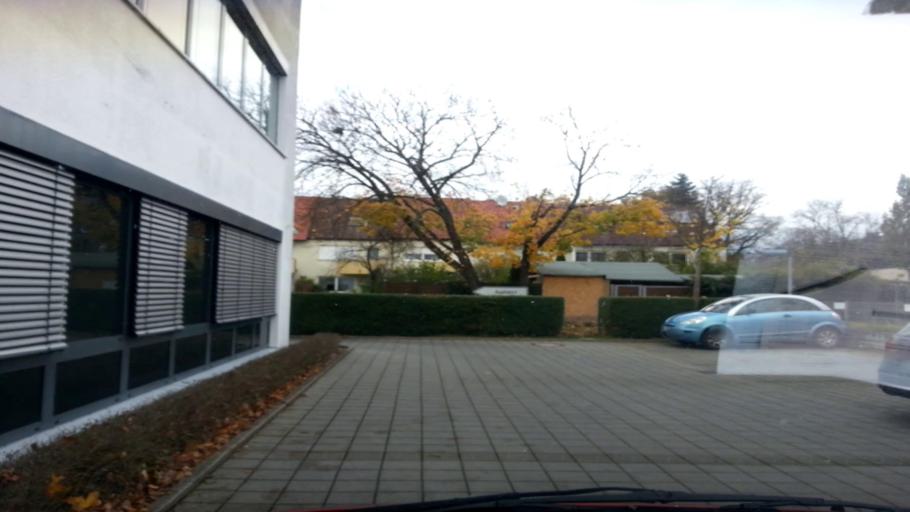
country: DE
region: Bavaria
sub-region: Upper Franconia
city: Bamberg
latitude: 49.8924
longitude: 10.9262
